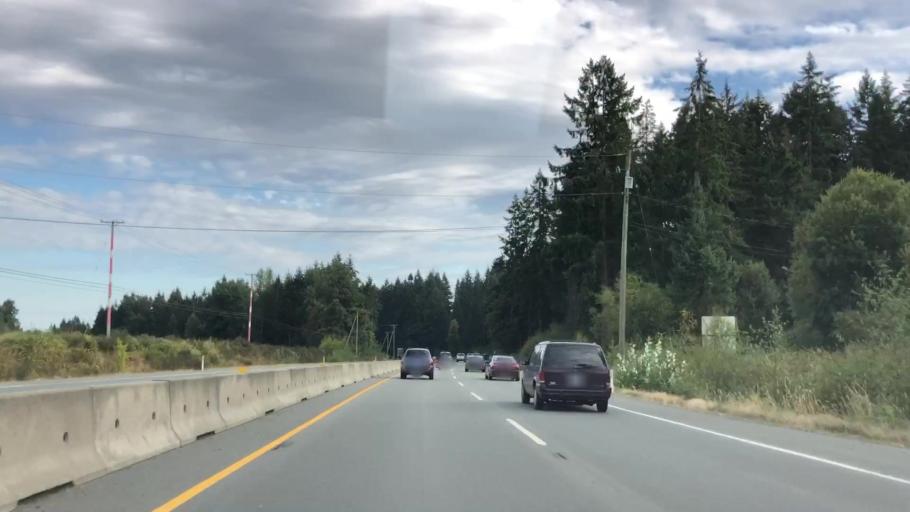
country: CA
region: British Columbia
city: Duncan
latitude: 48.7243
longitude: -123.6355
